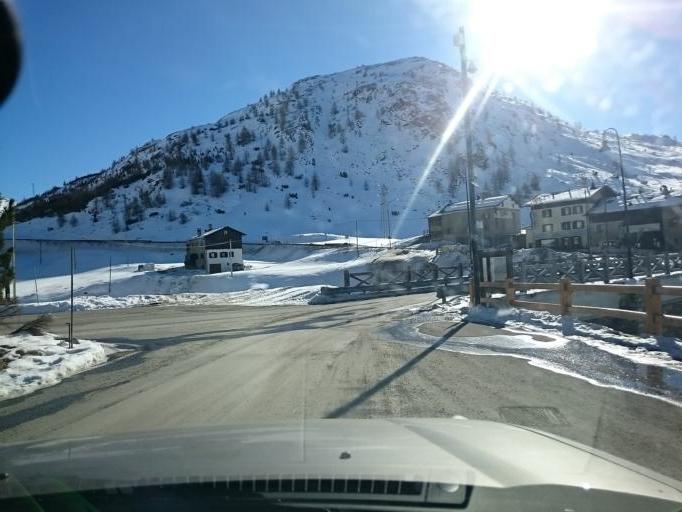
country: IT
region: Lombardy
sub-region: Provincia di Sondrio
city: Livigno
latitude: 46.5179
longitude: 10.1867
